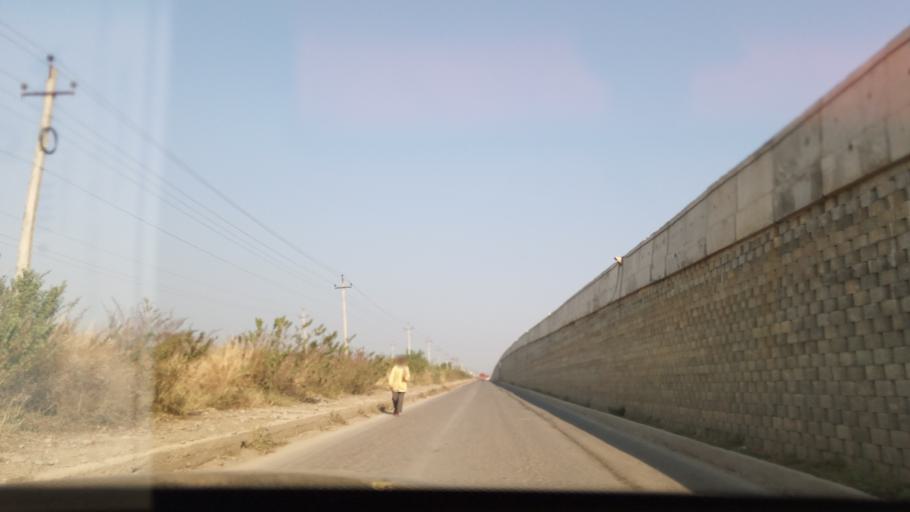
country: IN
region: Karnataka
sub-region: Haveri
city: Savanur
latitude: 14.8817
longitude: 75.3084
